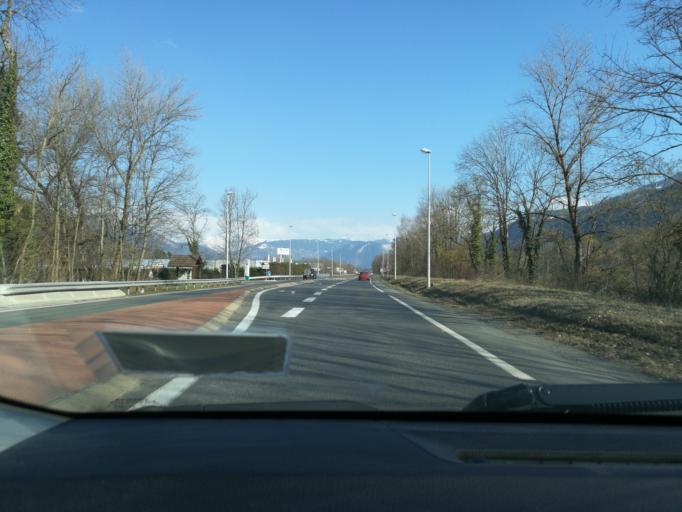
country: FR
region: Rhone-Alpes
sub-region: Departement de la Haute-Savoie
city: Ayse
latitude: 46.0749
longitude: 6.4448
